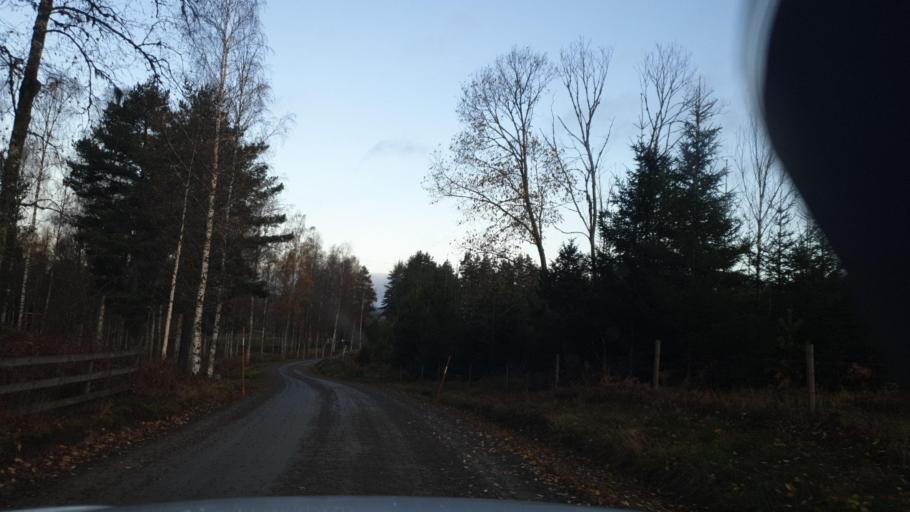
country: SE
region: Vaermland
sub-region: Arvika Kommun
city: Arvika
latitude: 59.5780
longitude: 12.7359
